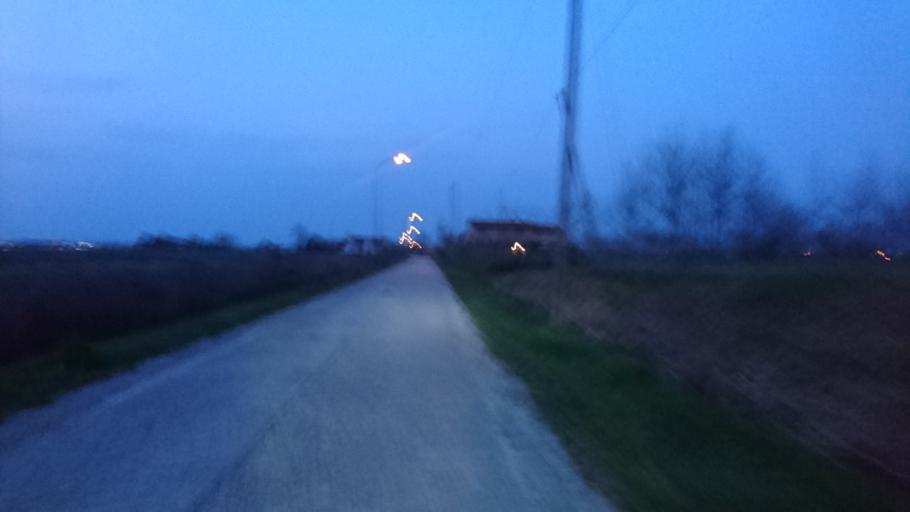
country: IT
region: Veneto
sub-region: Provincia di Padova
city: Abano Terme
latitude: 45.3707
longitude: 11.7844
